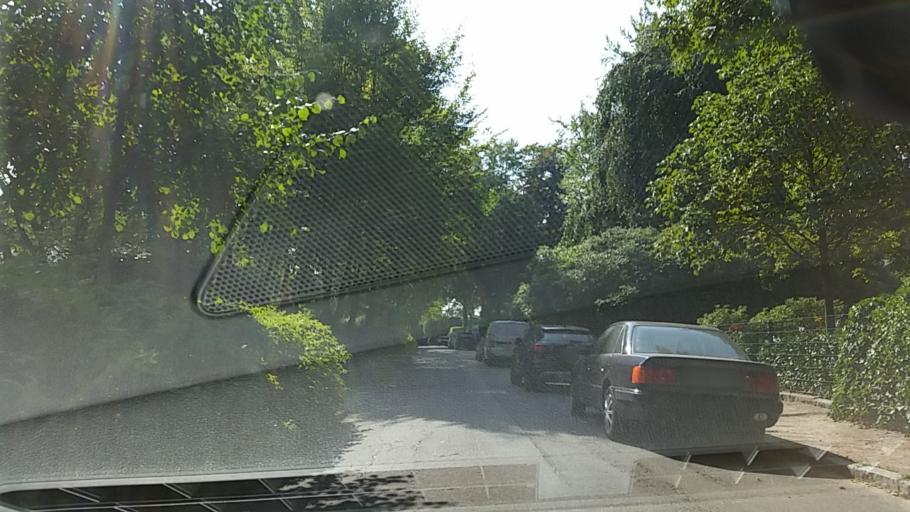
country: DE
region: Schleswig-Holstein
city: Halstenbek
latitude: 53.5552
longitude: 9.8320
